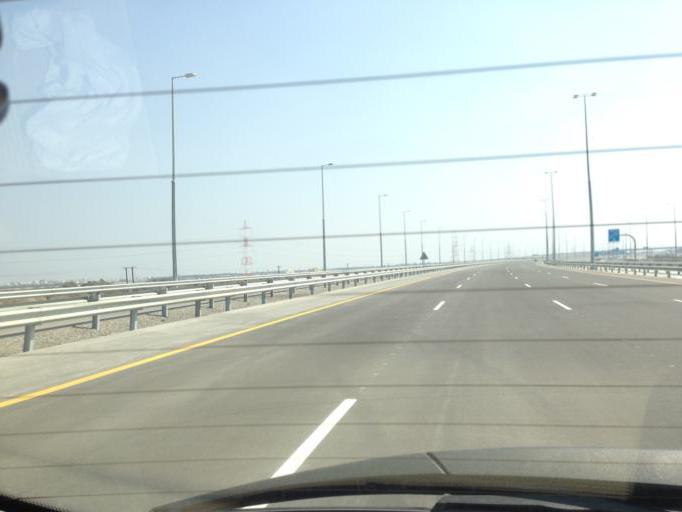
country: OM
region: Al Batinah
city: Barka'
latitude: 23.6324
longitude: 57.8600
